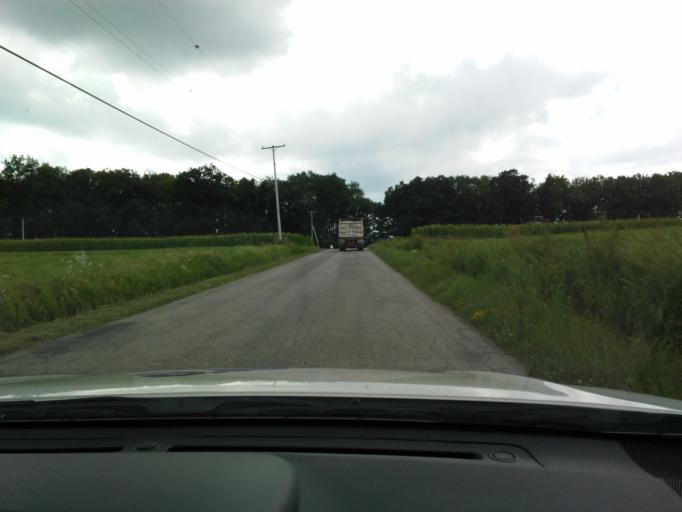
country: US
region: Pennsylvania
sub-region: Mercer County
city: Grove City
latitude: 41.2168
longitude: -80.0392
